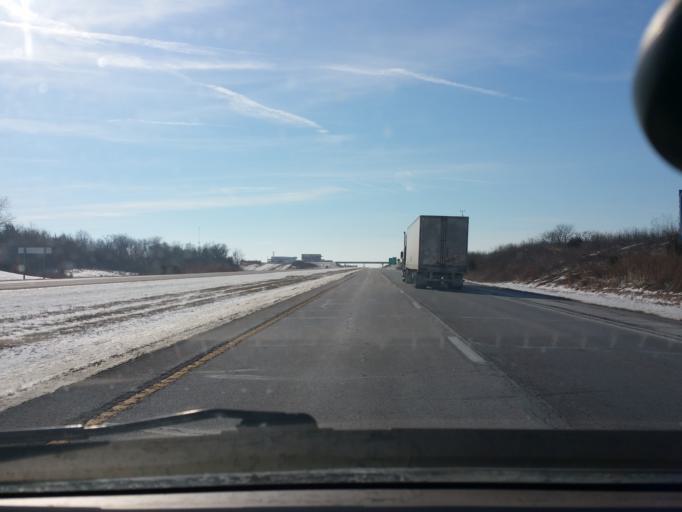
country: US
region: Iowa
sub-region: Decatur County
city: Lamoni
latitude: 40.4756
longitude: -93.9745
